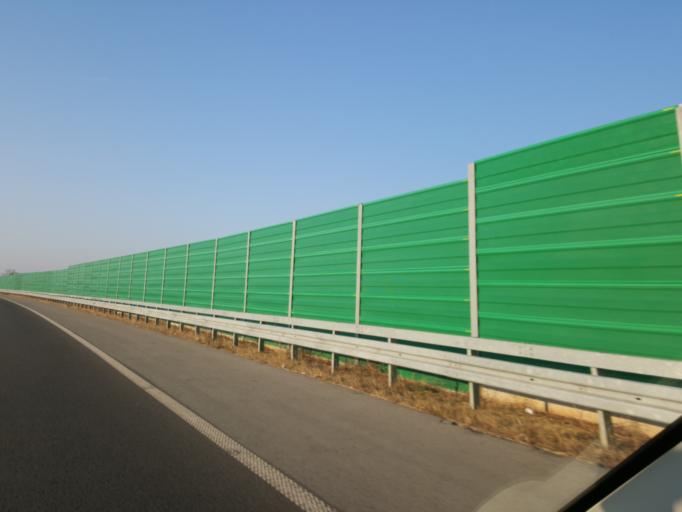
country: RS
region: Central Serbia
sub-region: Pirotski Okrug
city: Dimitrovgrad
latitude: 43.0453
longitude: 22.7069
